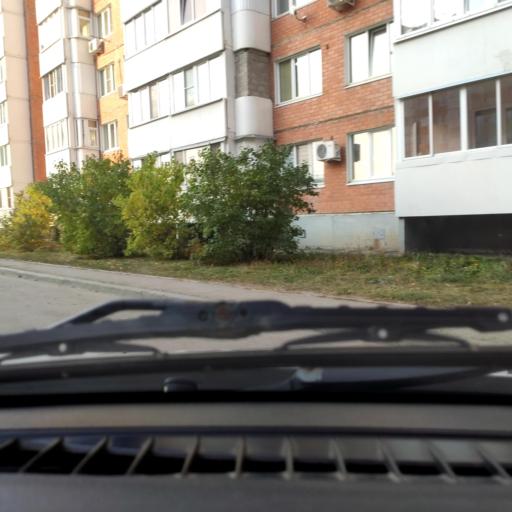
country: RU
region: Samara
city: Tol'yatti
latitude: 53.5423
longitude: 49.4022
